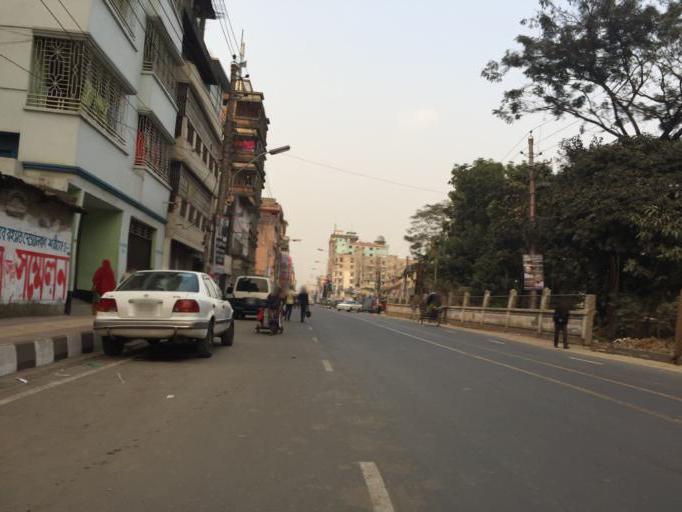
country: BD
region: Dhaka
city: Azimpur
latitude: 23.7841
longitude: 90.3472
